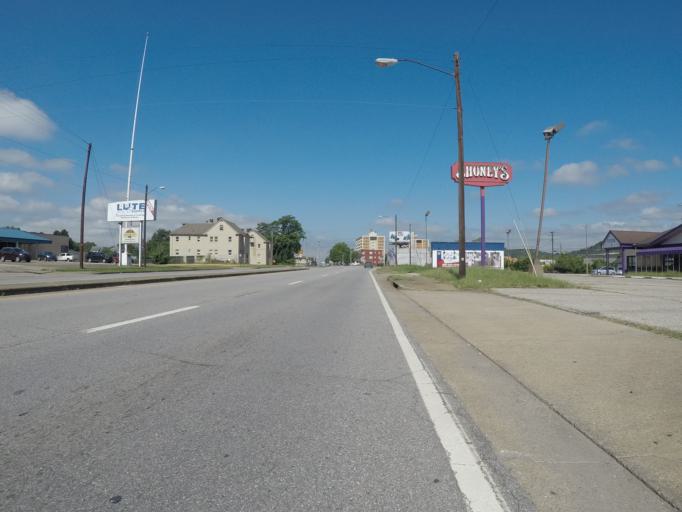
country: US
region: Kentucky
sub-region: Boyd County
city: Ashland
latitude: 38.4658
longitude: -82.6179
